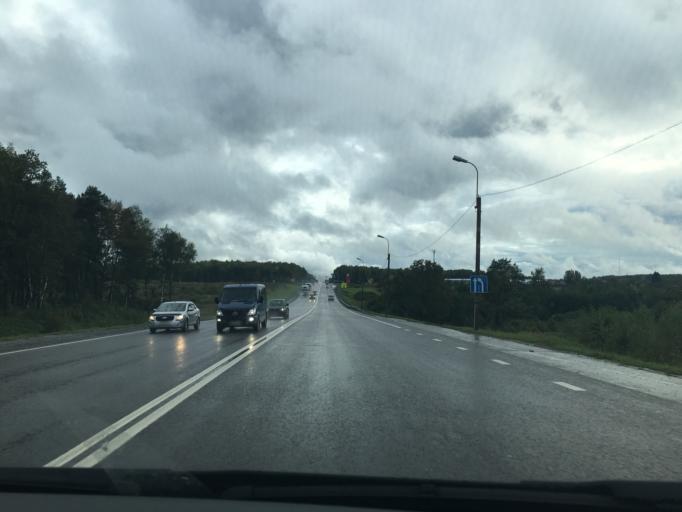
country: RU
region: Kaluga
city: Balabanovo
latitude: 55.1535
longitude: 36.6636
